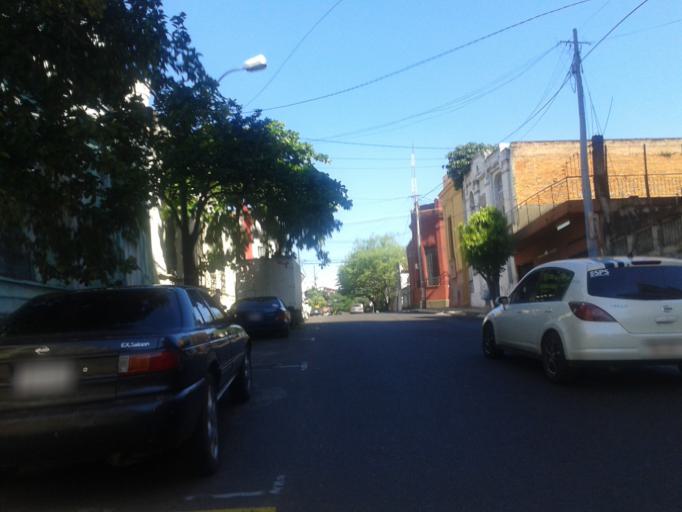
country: PY
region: Asuncion
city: Asuncion
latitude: -25.2894
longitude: -57.6390
